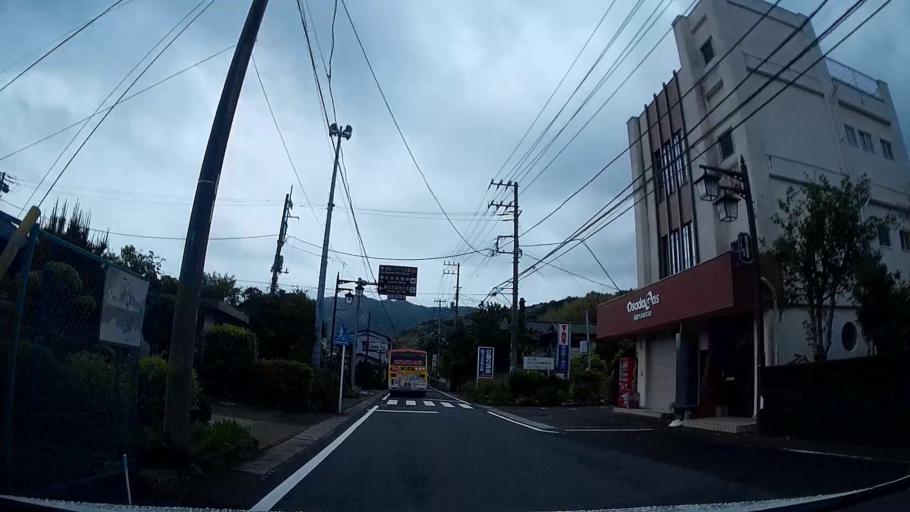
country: JP
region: Shizuoka
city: Shimoda
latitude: 34.7585
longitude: 138.9830
